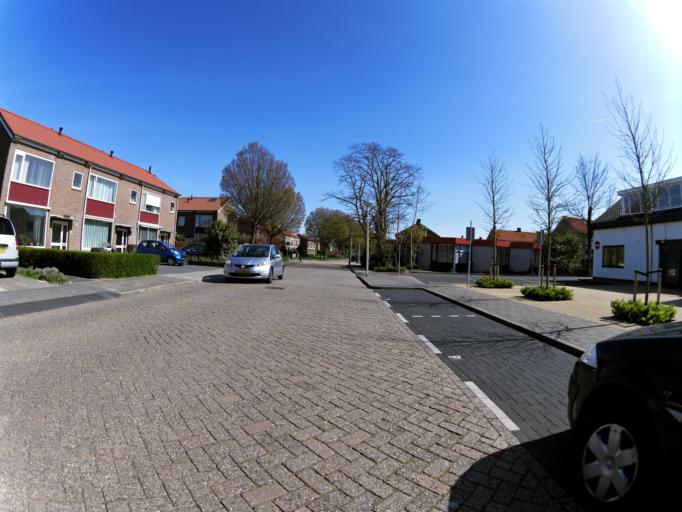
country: NL
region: South Holland
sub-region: Gemeente Brielle
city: Brielle
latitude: 51.9119
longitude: 4.1019
